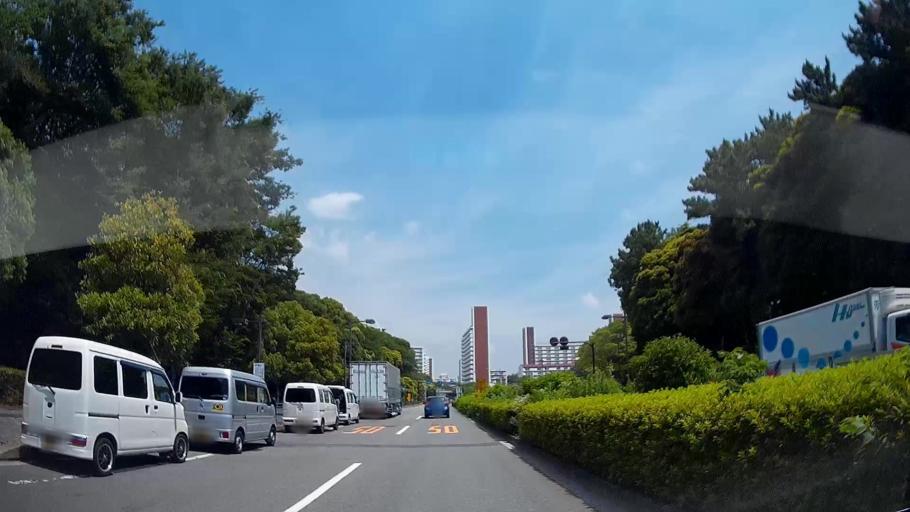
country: JP
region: Kanagawa
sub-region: Kawasaki-shi
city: Kawasaki
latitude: 35.5937
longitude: 139.7509
